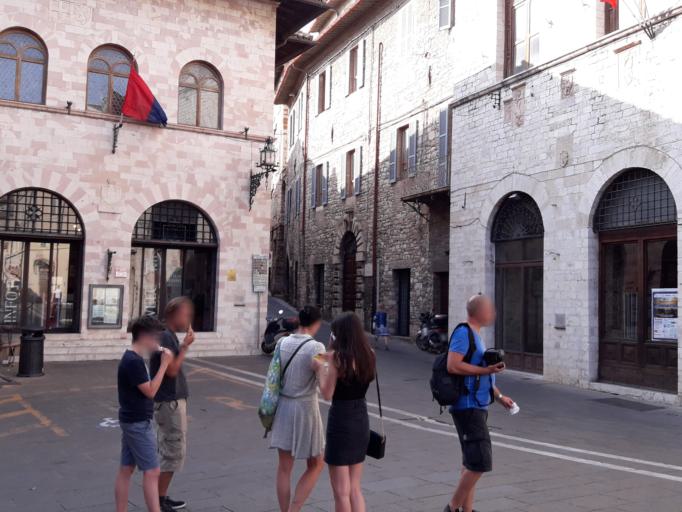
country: IT
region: Umbria
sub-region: Provincia di Perugia
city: Assisi
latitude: 43.0712
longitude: 12.6145
